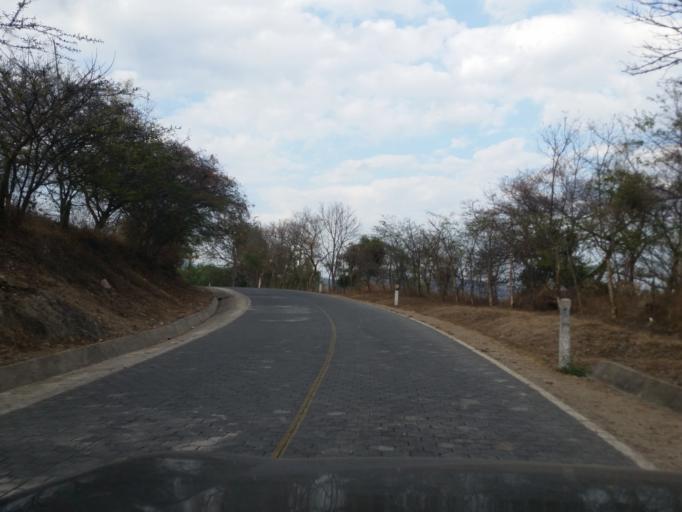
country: NI
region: Jinotega
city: La Concordia
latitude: 13.1916
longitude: -86.1696
